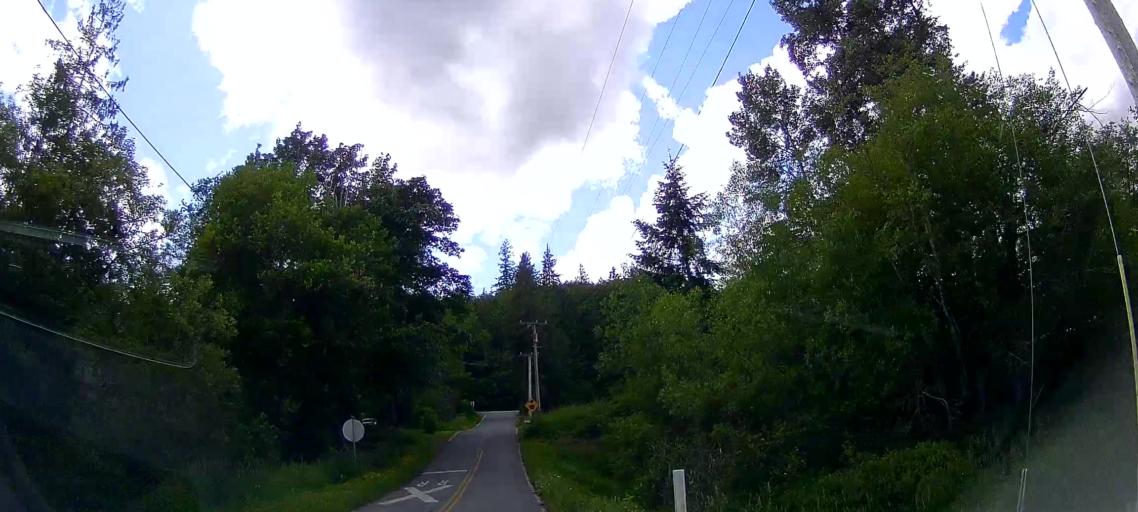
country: US
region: Washington
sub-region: Whatcom County
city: Sudden Valley
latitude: 48.6924
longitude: -122.1905
